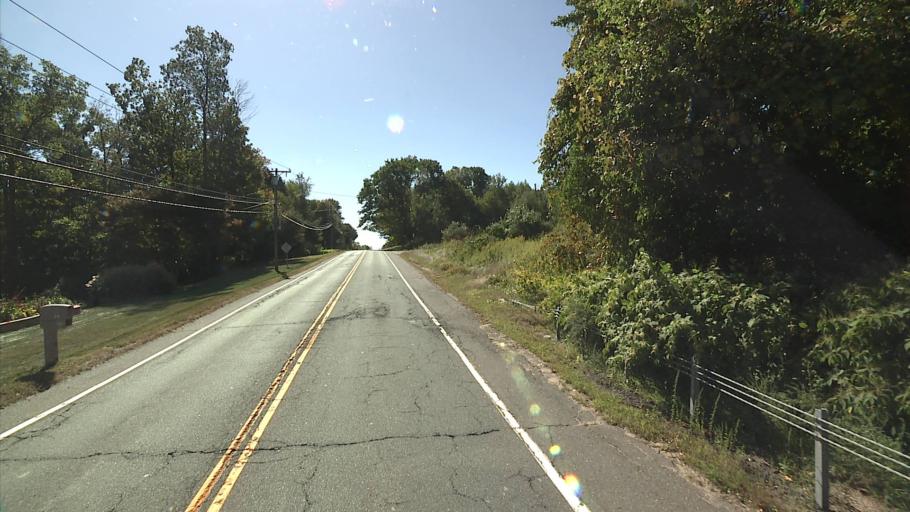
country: US
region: Connecticut
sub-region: New Haven County
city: Prospect
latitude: 41.4738
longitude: -72.9684
